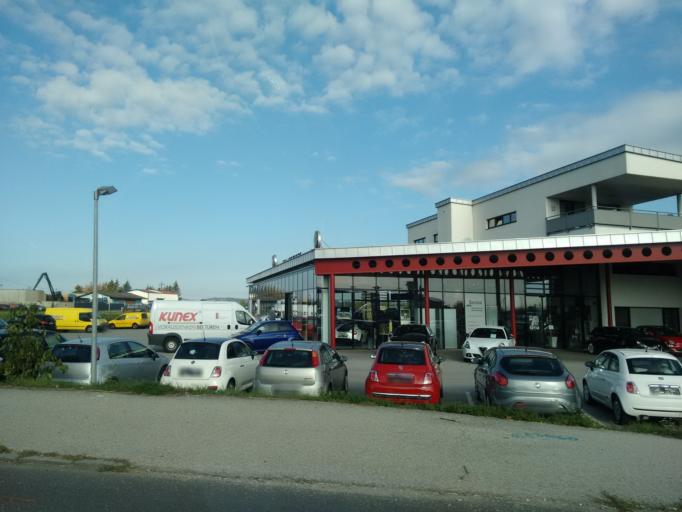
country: AT
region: Upper Austria
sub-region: Politischer Bezirk Linz-Land
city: Horsching
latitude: 48.2021
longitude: 14.1542
